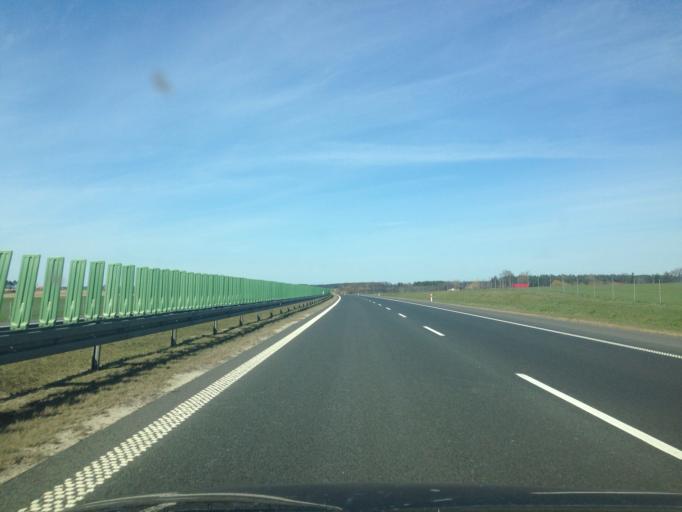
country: PL
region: Pomeranian Voivodeship
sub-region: Powiat starogardzki
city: Smetowo Graniczne
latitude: 53.7607
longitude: 18.6354
